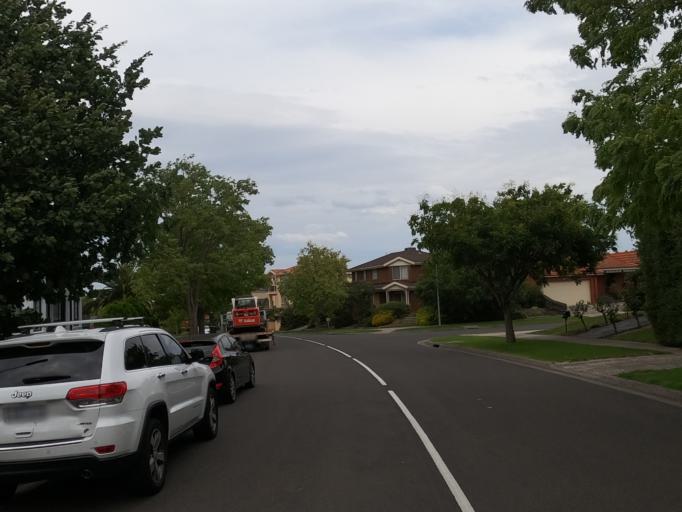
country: AU
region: Victoria
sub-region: Hume
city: Meadow Heights
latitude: -37.6479
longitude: 144.9023
